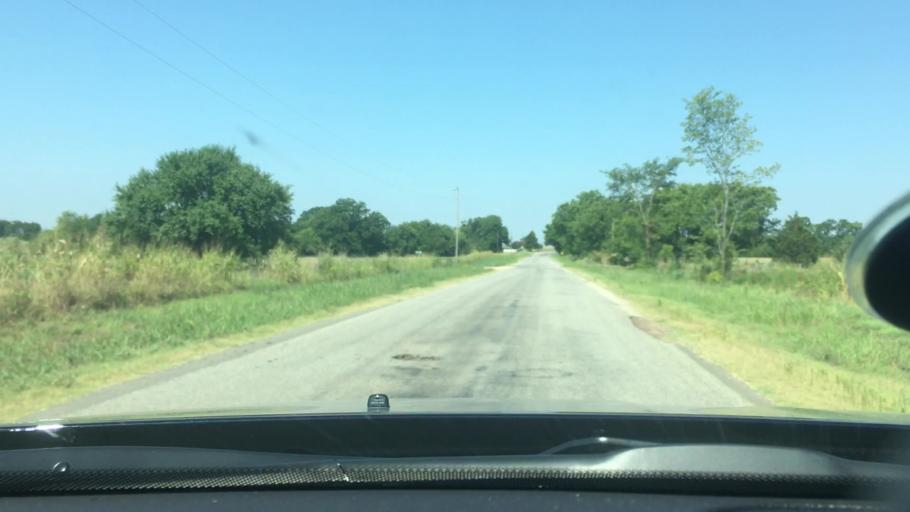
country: US
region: Oklahoma
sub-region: Johnston County
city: Tishomingo
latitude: 34.3104
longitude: -96.6306
